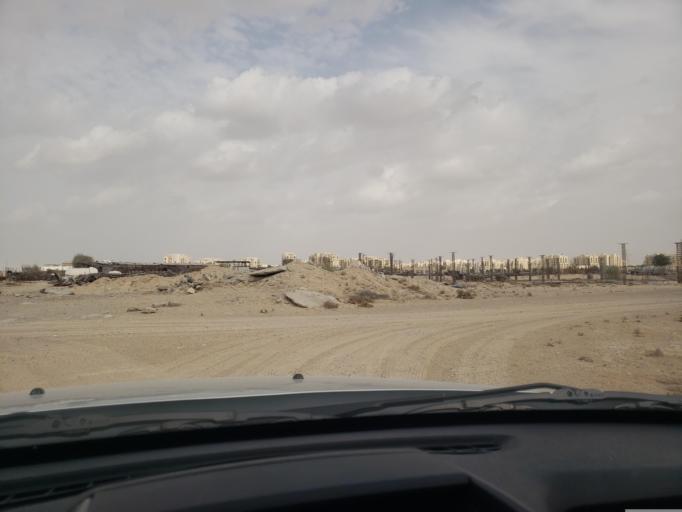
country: AE
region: Dubai
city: Dubai
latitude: 24.9990
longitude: 55.2403
